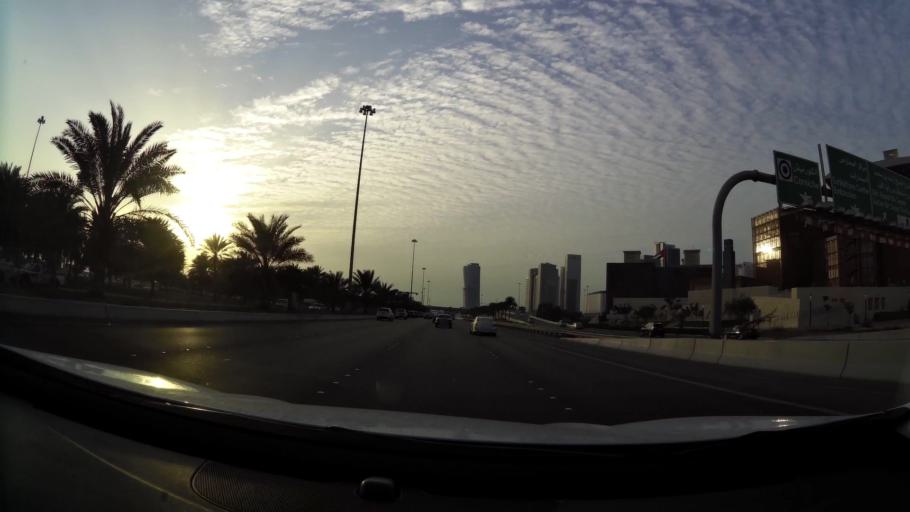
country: AE
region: Abu Dhabi
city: Abu Dhabi
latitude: 24.4142
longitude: 54.4476
